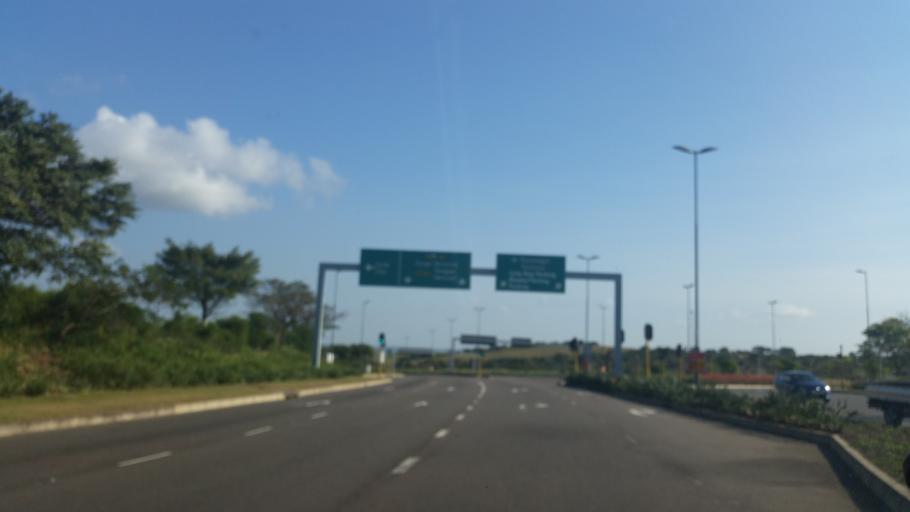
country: ZA
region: KwaZulu-Natal
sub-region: iLembe District Municipality
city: Ballitoville
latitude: -29.6227
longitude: 31.1000
